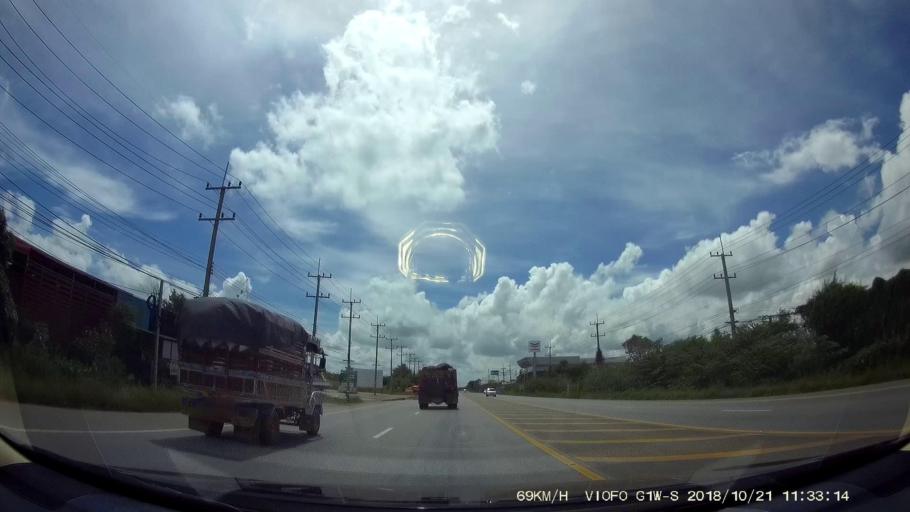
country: TH
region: Chaiyaphum
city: Chaiyaphum
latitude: 15.7483
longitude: 102.0241
